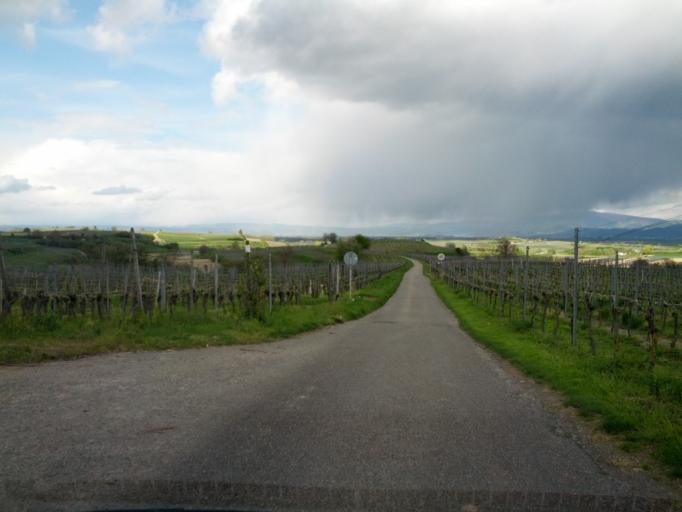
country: DE
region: Baden-Wuerttemberg
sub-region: Freiburg Region
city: Merdingen
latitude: 47.9987
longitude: 7.6825
